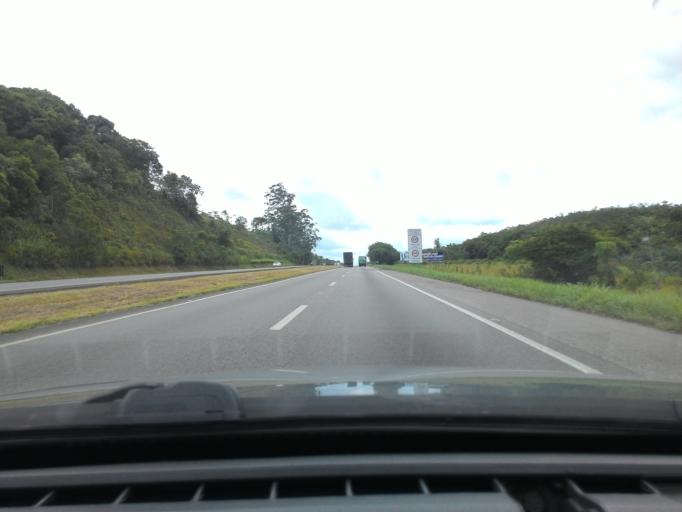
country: BR
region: Sao Paulo
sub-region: Registro
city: Registro
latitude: -24.5587
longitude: -47.8664
